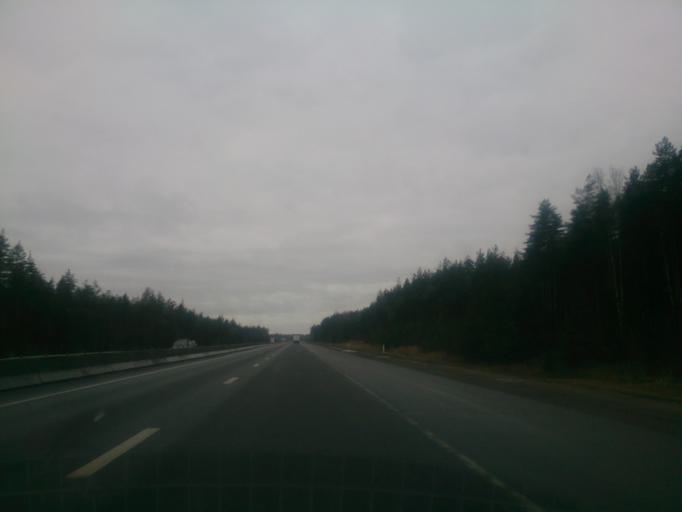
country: RU
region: Leningrad
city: Tosno
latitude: 59.4922
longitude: 30.9423
